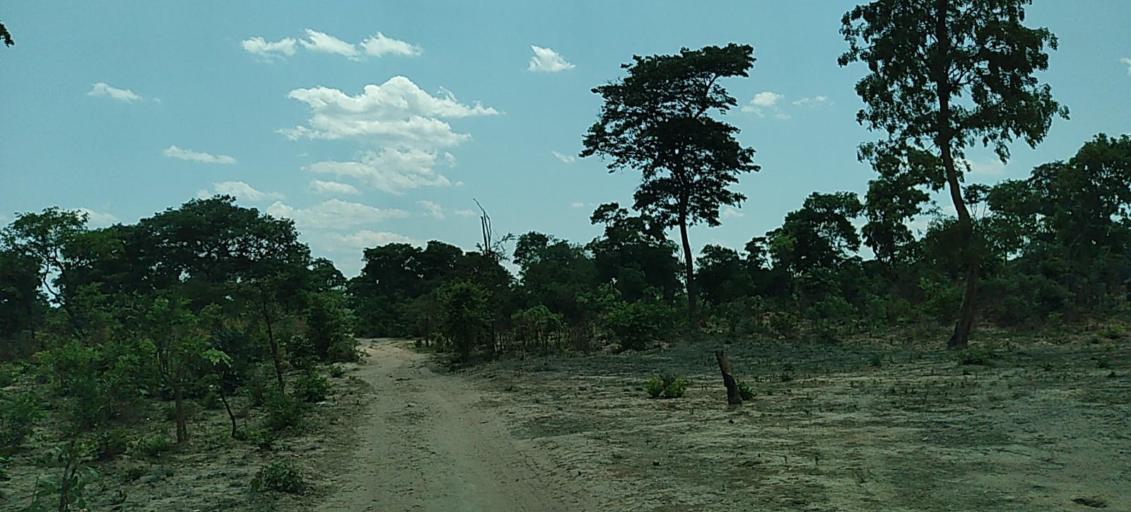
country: ZM
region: Central
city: Kapiri Mposhi
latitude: -13.6336
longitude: 28.7553
